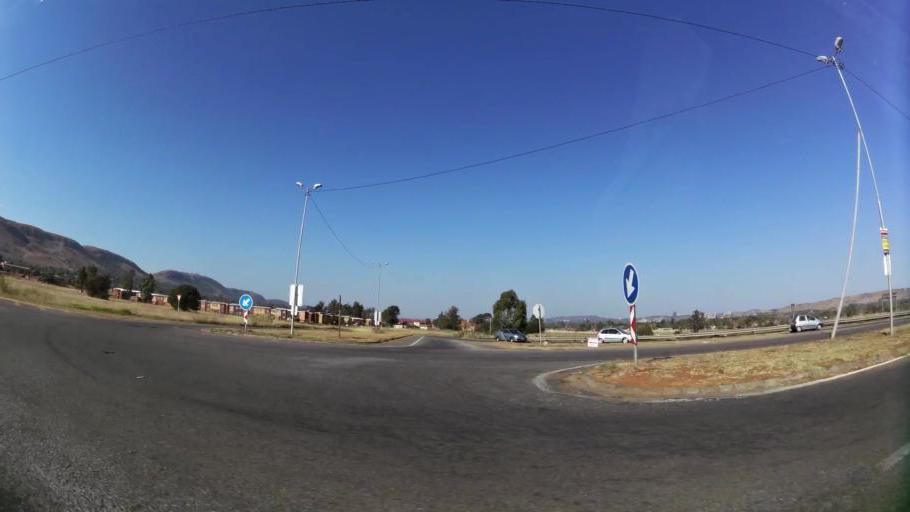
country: ZA
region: Gauteng
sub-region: City of Tshwane Metropolitan Municipality
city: Pretoria
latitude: -25.7019
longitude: 28.1383
